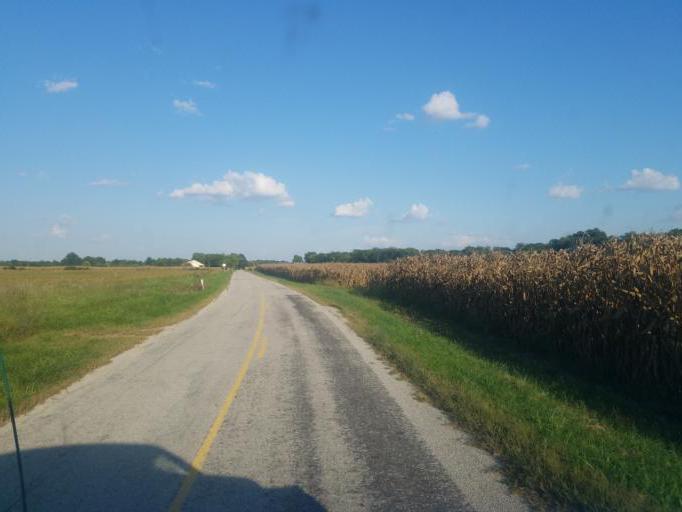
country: US
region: Ohio
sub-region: Wyandot County
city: Upper Sandusky
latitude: 40.6728
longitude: -83.3507
